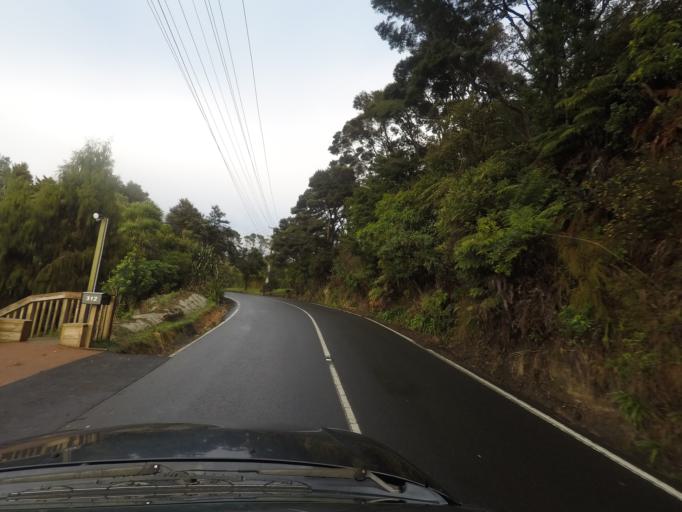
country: NZ
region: Auckland
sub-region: Auckland
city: Titirangi
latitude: -36.9241
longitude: 174.5831
